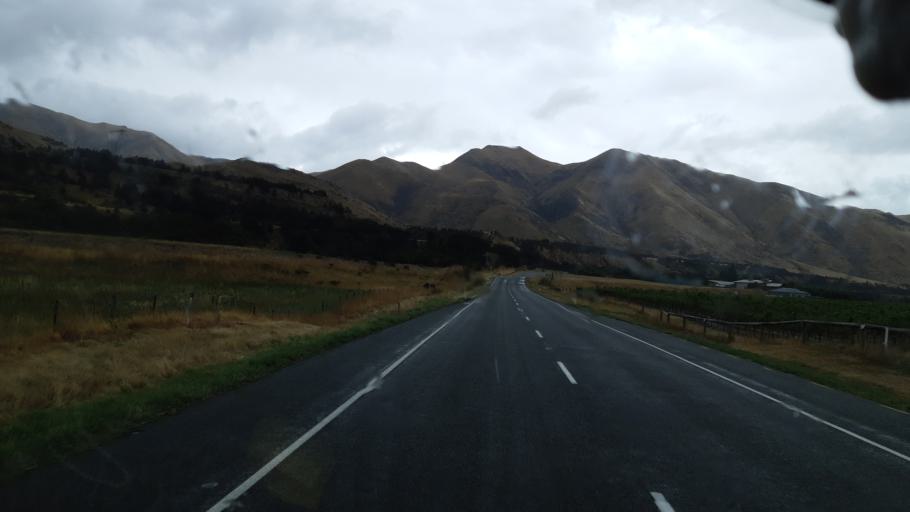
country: NZ
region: Canterbury
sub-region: Hurunui District
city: Amberley
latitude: -42.6234
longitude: 172.7644
